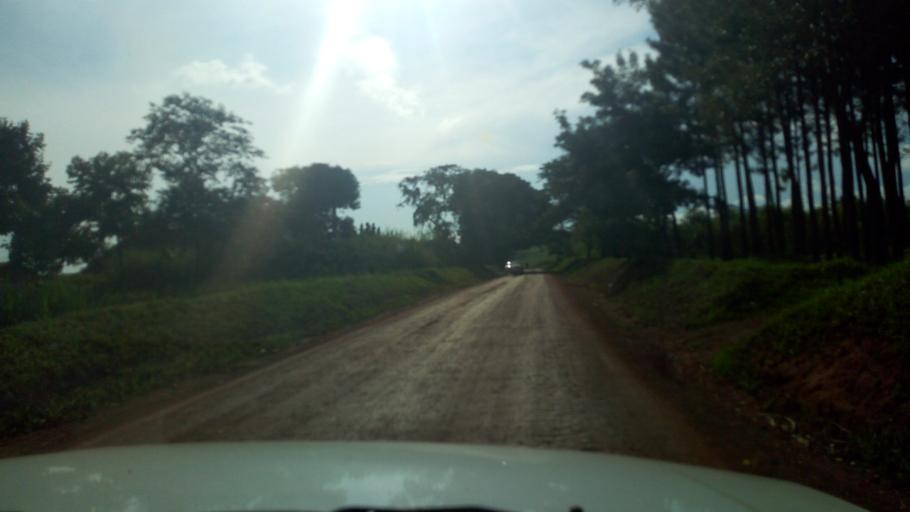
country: UG
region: Western Region
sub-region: Masindi District
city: Masindi
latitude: 1.6740
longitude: 31.6589
